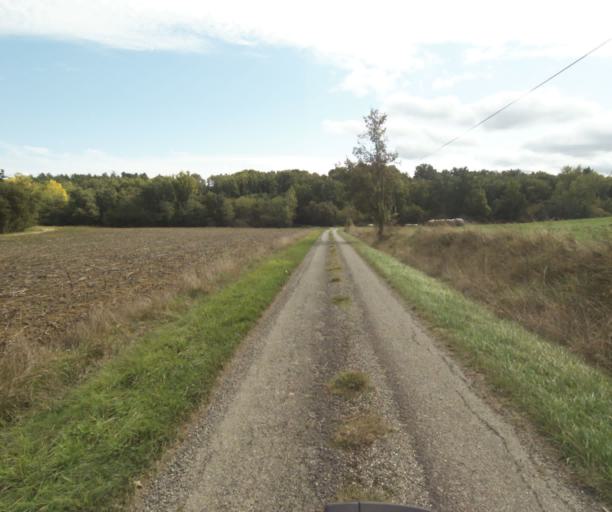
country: FR
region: Midi-Pyrenees
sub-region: Departement du Tarn-et-Garonne
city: Verdun-sur-Garonne
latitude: 43.8668
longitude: 1.1887
